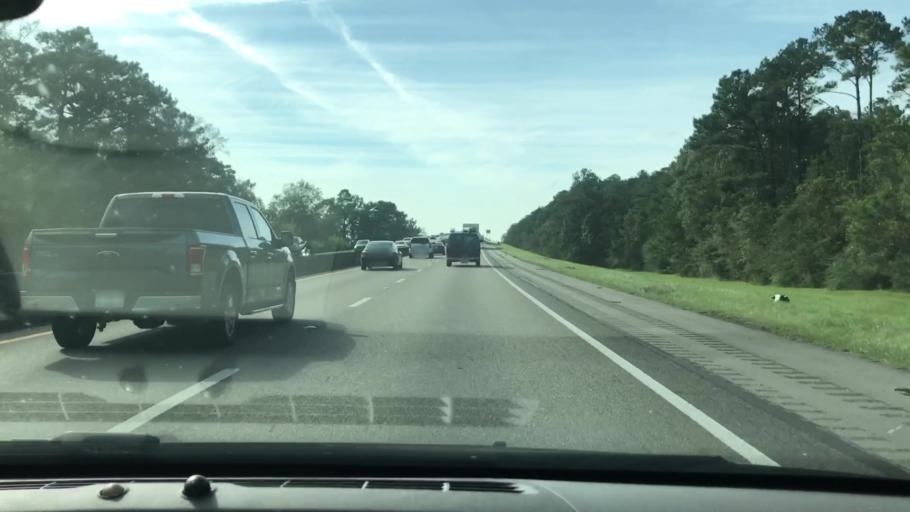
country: US
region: Mississippi
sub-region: Hancock County
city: Pearlington
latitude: 30.3057
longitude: -89.6320
